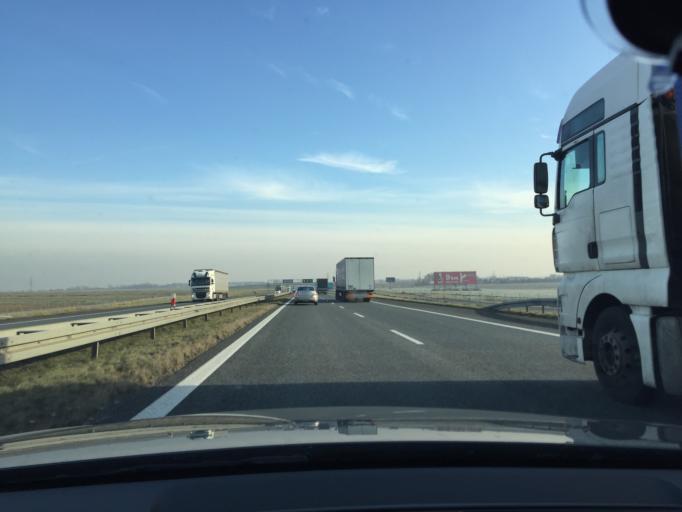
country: PL
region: Silesian Voivodeship
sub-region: Powiat gliwicki
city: Zernica
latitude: 50.2623
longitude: 18.6296
